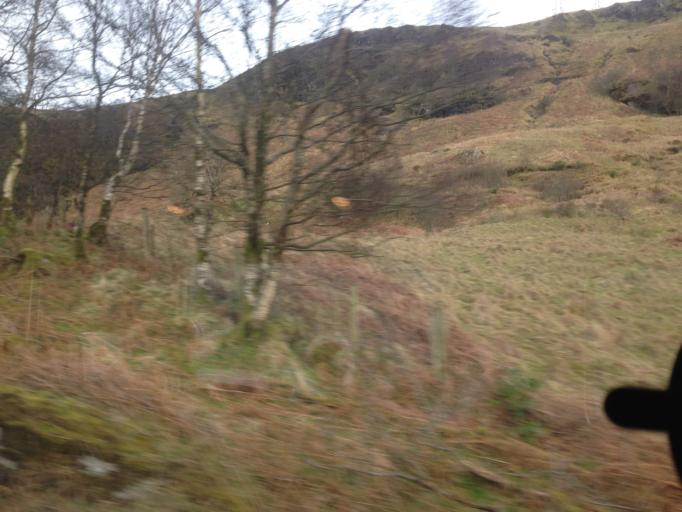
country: GB
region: Scotland
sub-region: Argyll and Bute
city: Garelochhead
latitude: 56.1772
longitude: -4.7739
